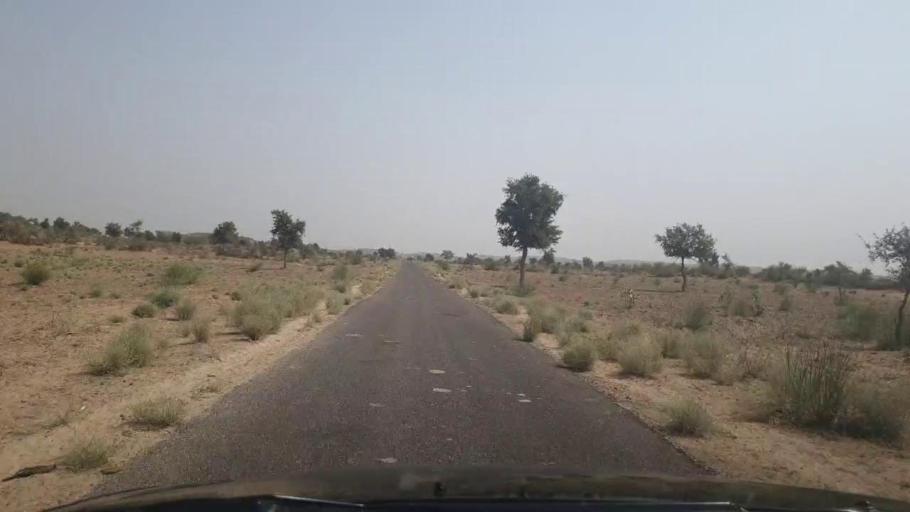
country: PK
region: Sindh
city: Islamkot
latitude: 24.9443
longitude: 70.3863
